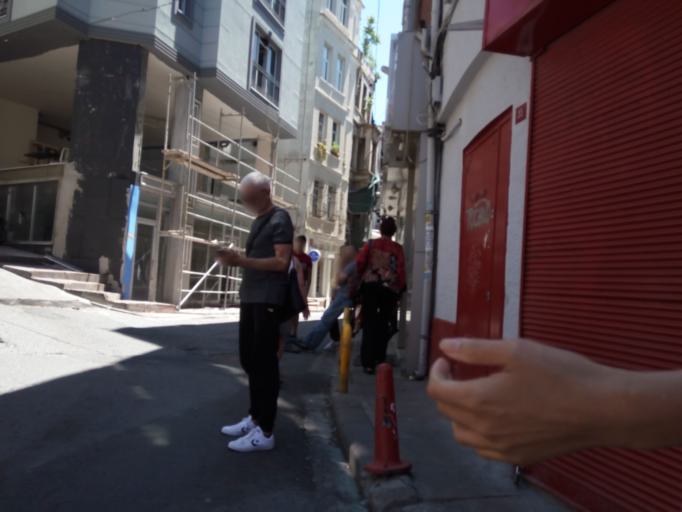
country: TR
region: Istanbul
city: Eminoenue
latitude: 41.0331
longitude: 28.9823
